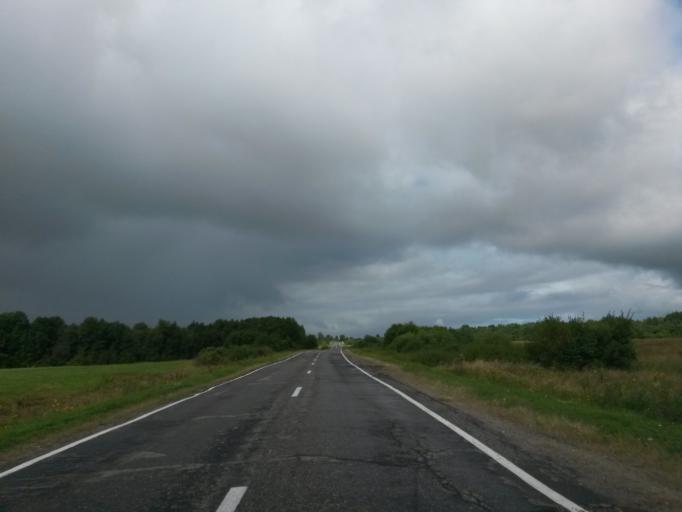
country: RU
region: Jaroslavl
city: Konstantinovskiy
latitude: 57.8367
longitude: 39.6587
